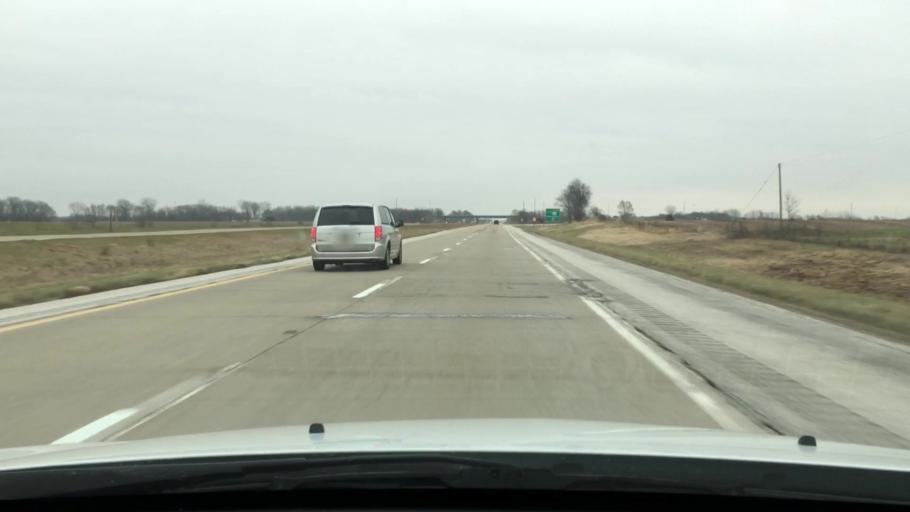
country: US
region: Illinois
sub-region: Scott County
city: Winchester
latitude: 39.6809
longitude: -90.4668
